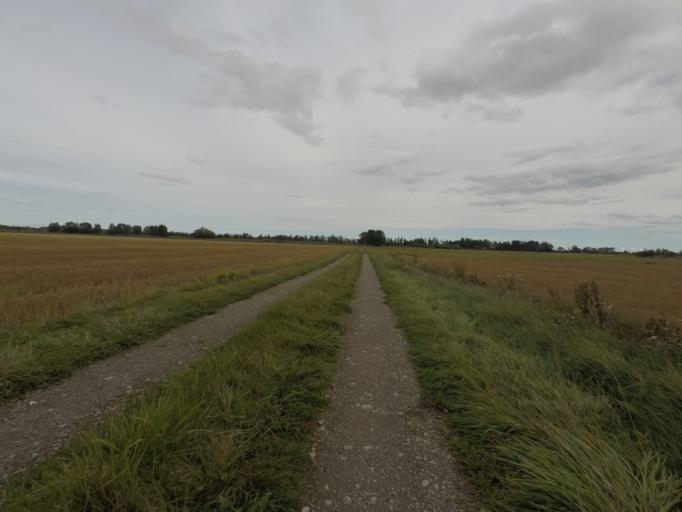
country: SE
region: Vaestmanland
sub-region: Kungsors Kommun
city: Kungsoer
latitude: 59.4589
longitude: 16.0552
